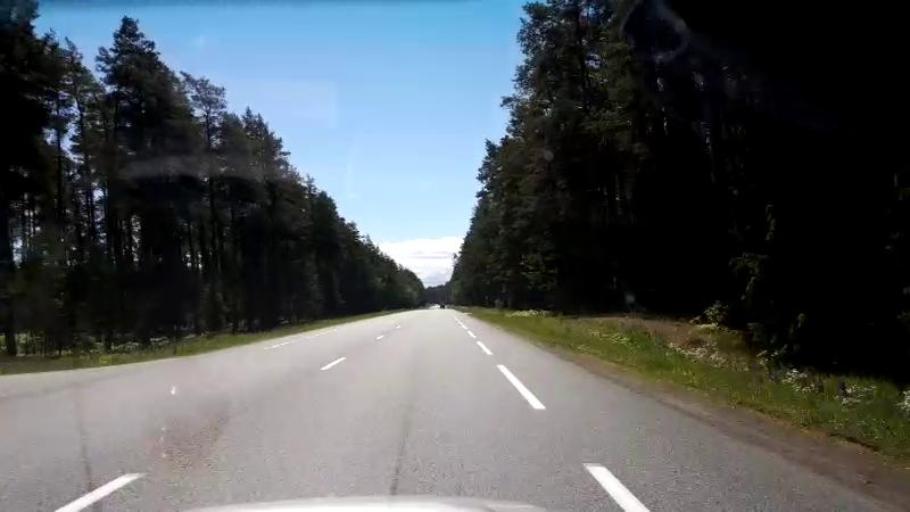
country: LV
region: Saulkrastu
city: Saulkrasti
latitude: 57.3557
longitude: 24.4381
